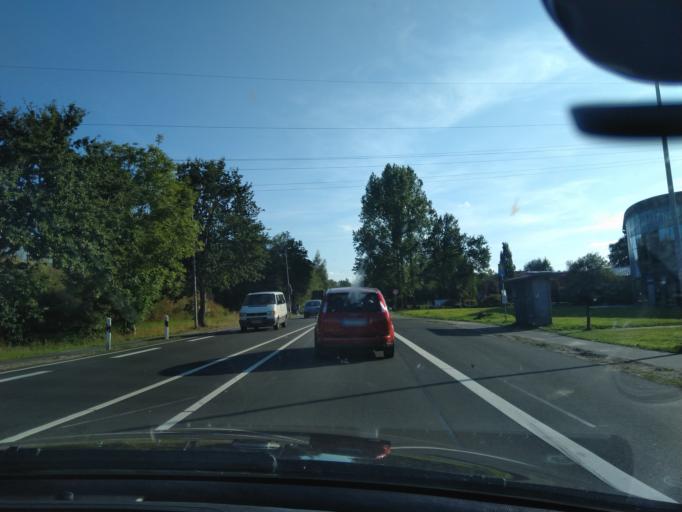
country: DE
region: Lower Saxony
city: Leer
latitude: 53.2581
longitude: 7.4591
